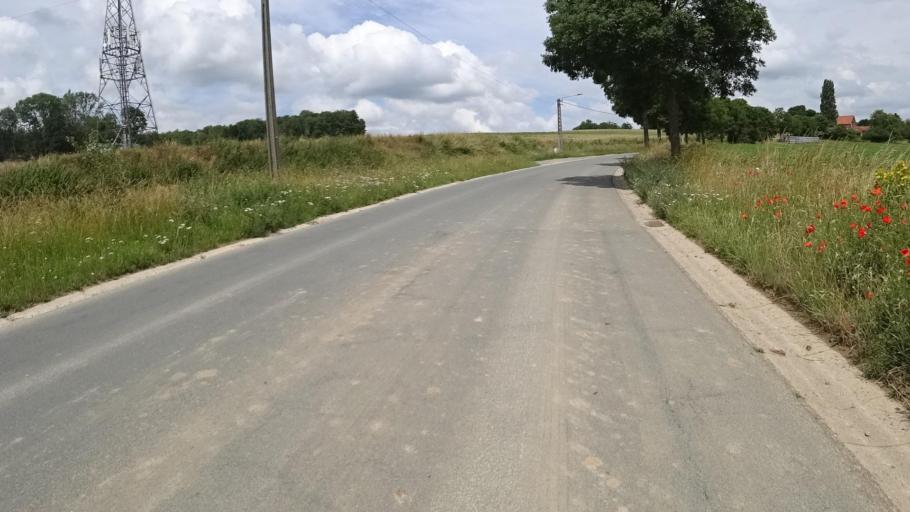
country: BE
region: Wallonia
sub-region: Province de Namur
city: Namur
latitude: 50.4874
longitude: 4.8678
